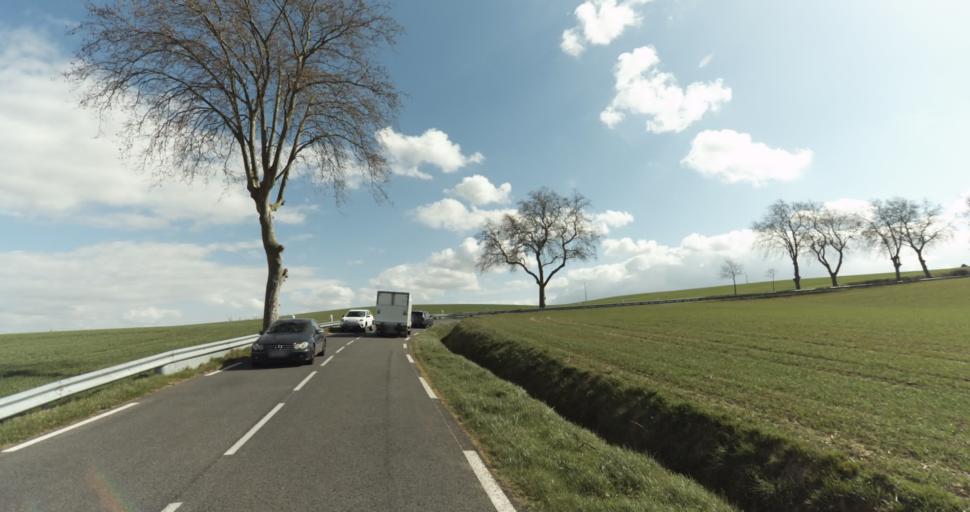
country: FR
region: Midi-Pyrenees
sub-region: Departement de la Haute-Garonne
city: Auterive
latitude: 43.3617
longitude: 1.5250
